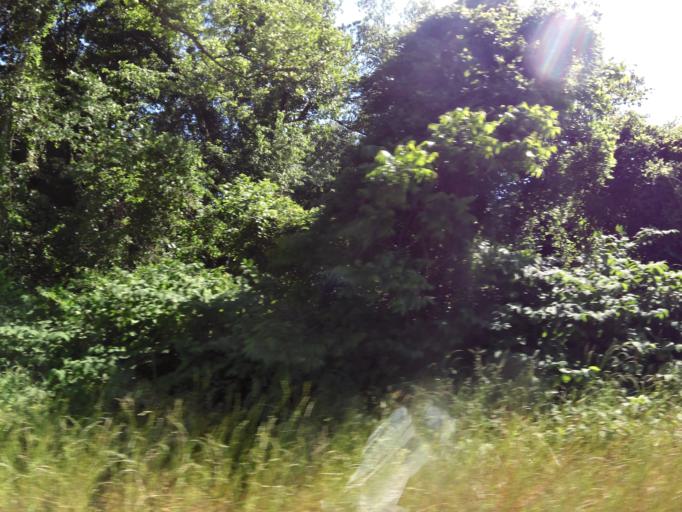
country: US
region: South Carolina
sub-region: Bamberg County
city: Denmark
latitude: 33.3340
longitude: -81.1600
